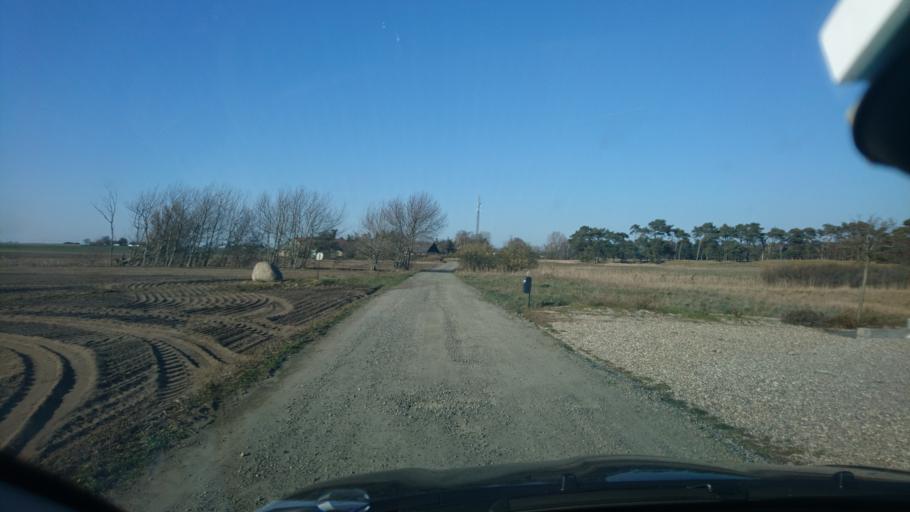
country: SE
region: Skane
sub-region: Simrishamns Kommun
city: Simrishamn
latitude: 55.4180
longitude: 14.2059
